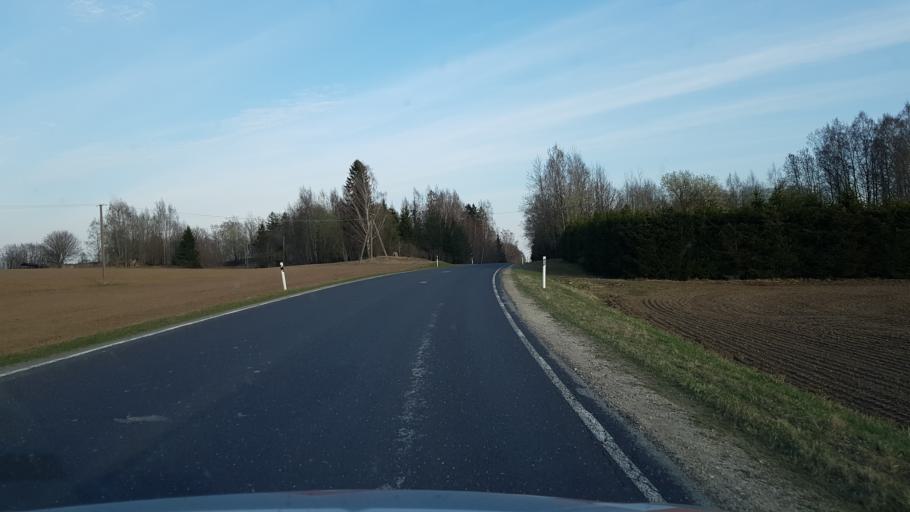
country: EE
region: Laeaene-Virumaa
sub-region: Vinni vald
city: Vinni
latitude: 59.3211
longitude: 26.5047
